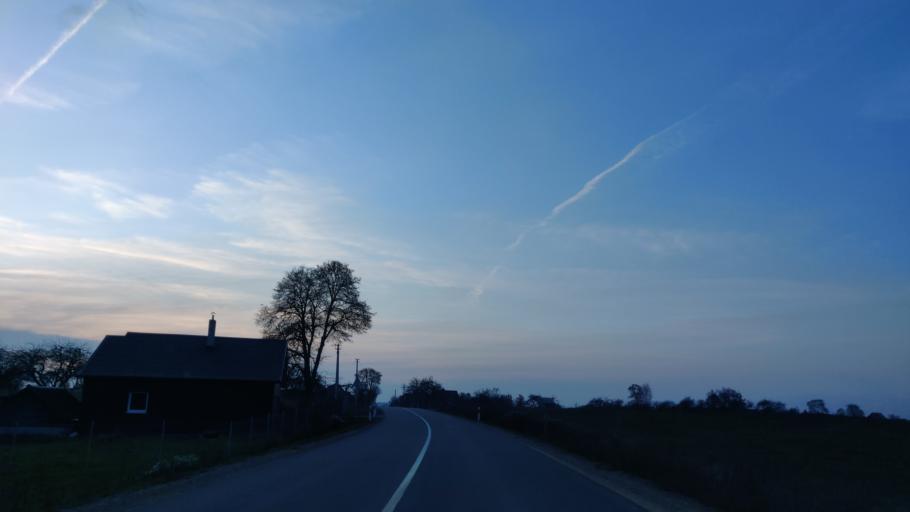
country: LT
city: Lentvaris
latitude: 54.5998
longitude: 25.0212
